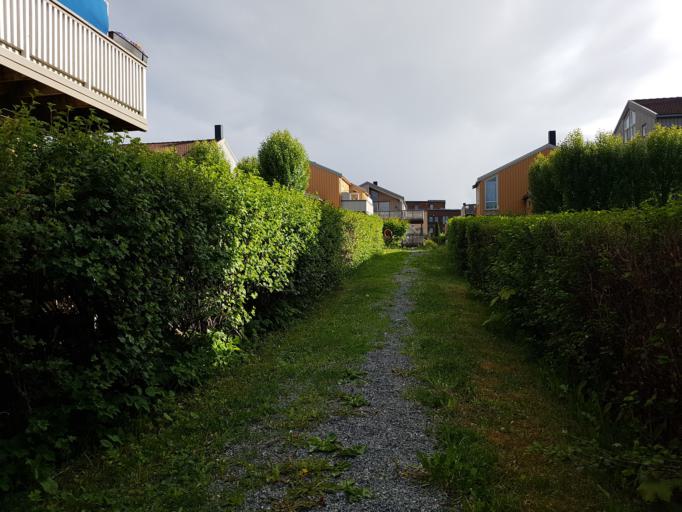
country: NO
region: Sor-Trondelag
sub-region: Trondheim
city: Trondheim
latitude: 63.4316
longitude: 10.4622
